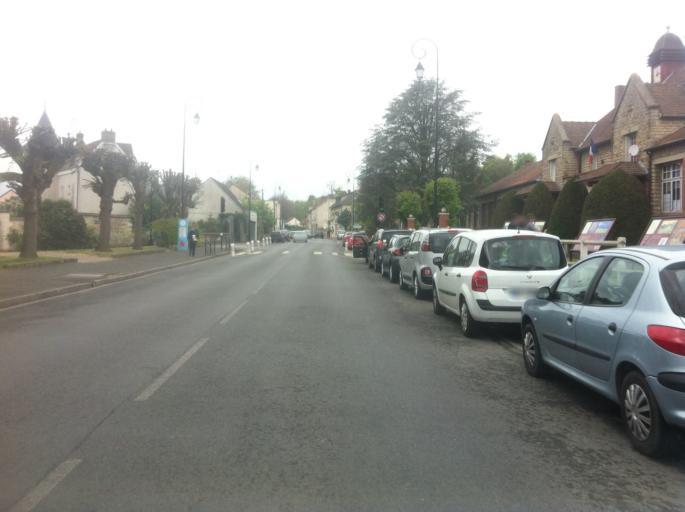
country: FR
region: Ile-de-France
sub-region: Departement du Val-d'Oise
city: Auvers-sur-Oise
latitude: 49.0707
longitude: 2.1710
